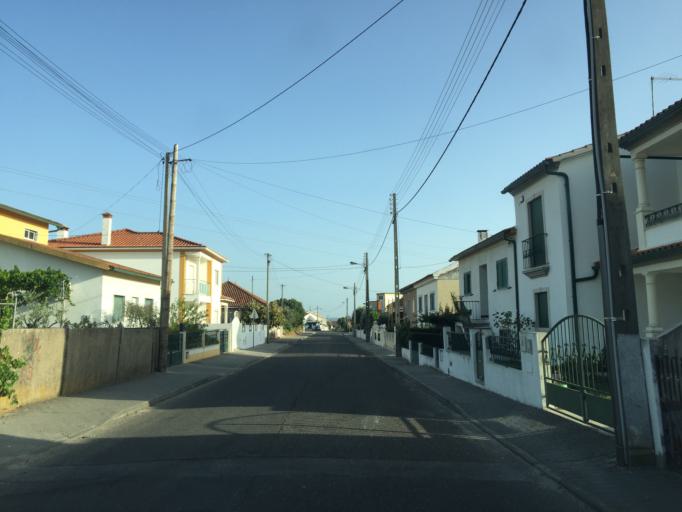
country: PT
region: Santarem
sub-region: Entroncamento
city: Entroncamento
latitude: 39.4790
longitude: -8.4521
